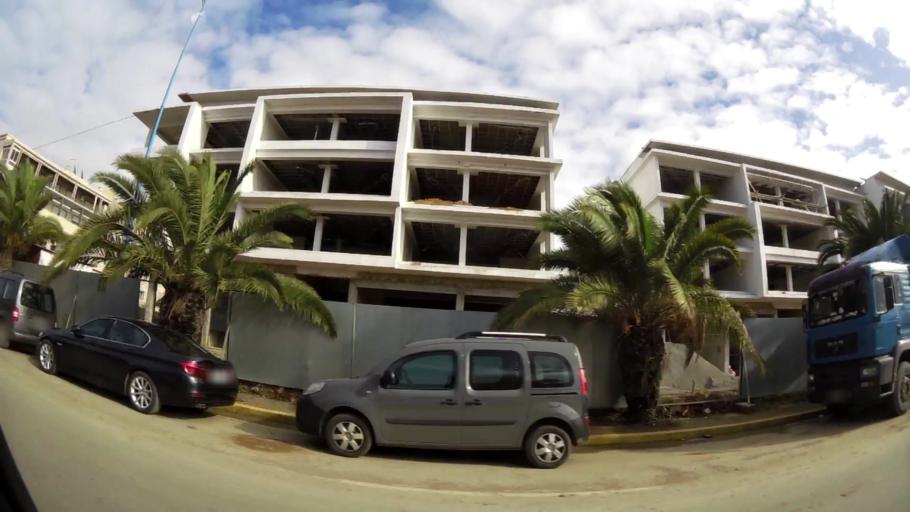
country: MA
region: Grand Casablanca
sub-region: Mohammedia
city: Mohammedia
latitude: 33.7121
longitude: -7.3436
